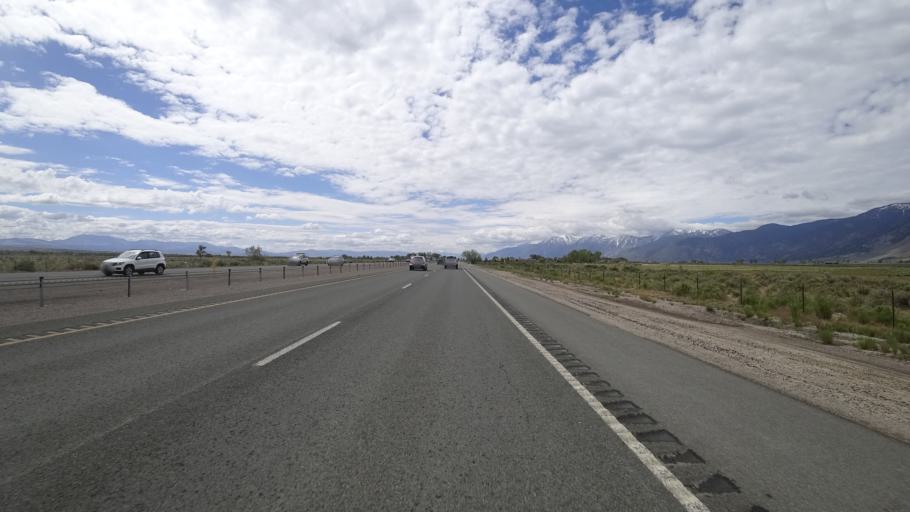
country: US
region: Nevada
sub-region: Douglas County
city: Indian Hills
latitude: 39.0638
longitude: -119.7802
